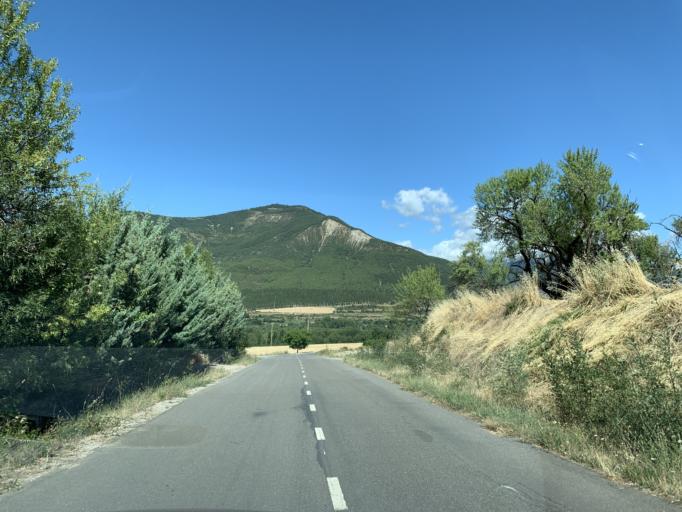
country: ES
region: Aragon
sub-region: Provincia de Huesca
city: Sabinanigo
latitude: 42.5515
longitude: -0.3172
